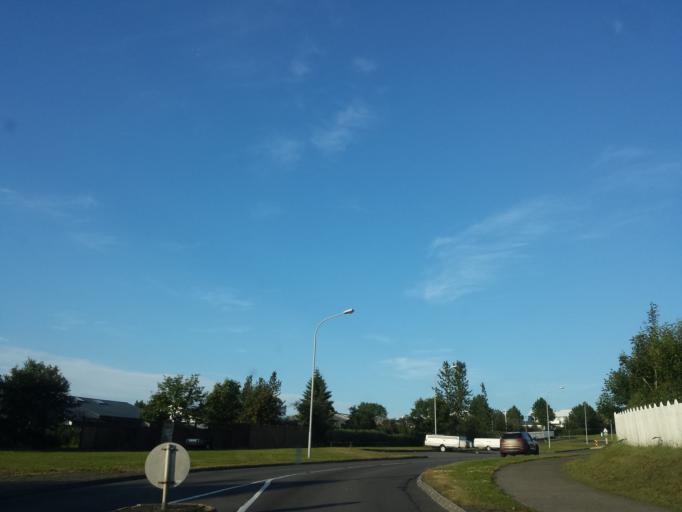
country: IS
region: Capital Region
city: Reykjavik
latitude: 64.1214
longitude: -21.8245
